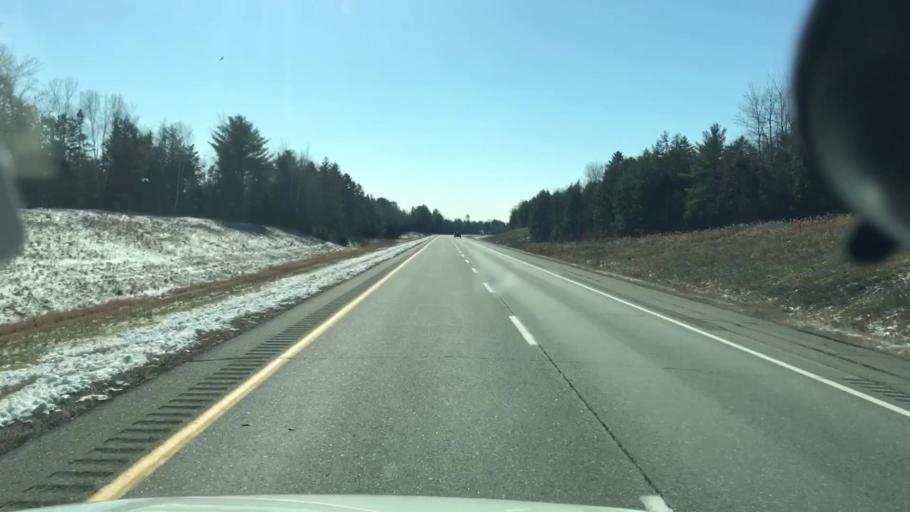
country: US
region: Maine
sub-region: Penobscot County
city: Howland
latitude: 45.2945
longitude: -68.6645
